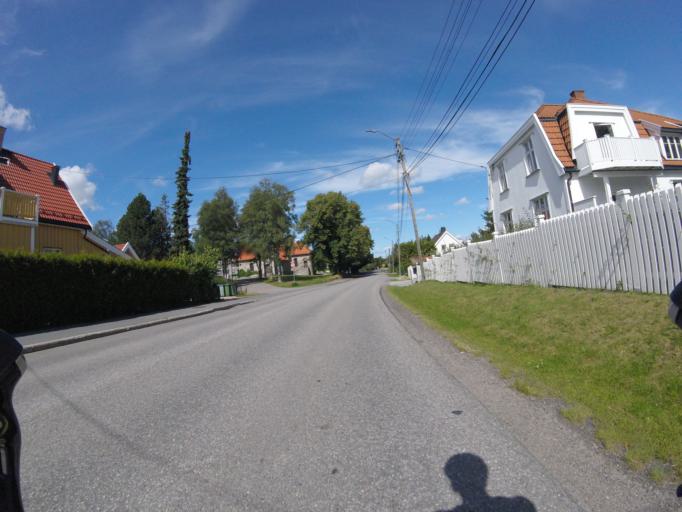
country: NO
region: Akershus
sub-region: Skedsmo
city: Lillestrom
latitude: 59.9518
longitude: 11.0157
